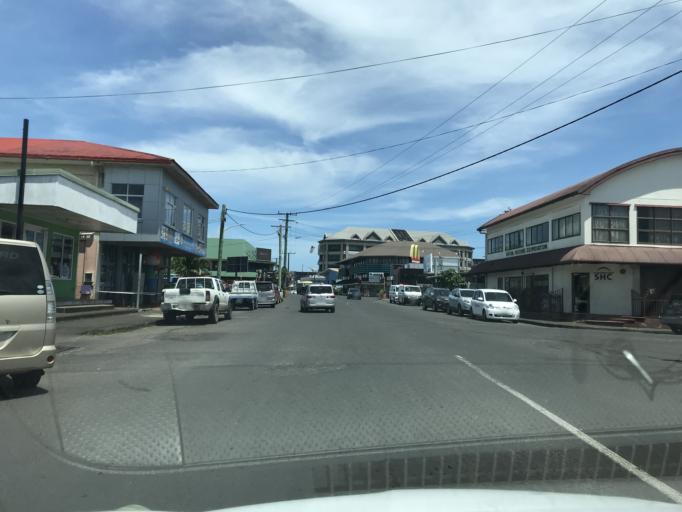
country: WS
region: Tuamasaga
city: Apia
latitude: -13.8321
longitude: -171.7681
